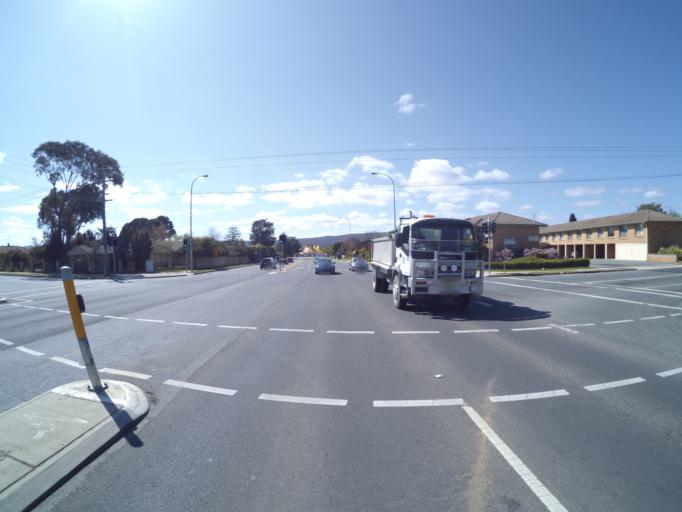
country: AU
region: New South Wales
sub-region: Queanbeyan
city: Queanbeyan
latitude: -35.3568
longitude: 149.2252
